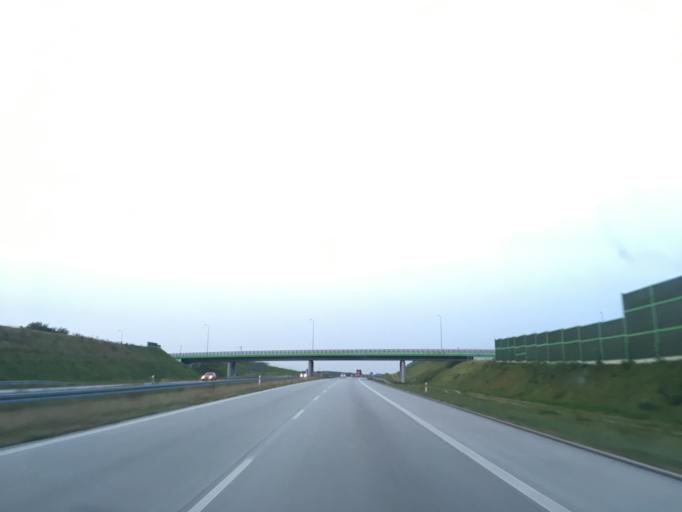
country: PL
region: Lodz Voivodeship
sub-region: Powiat zgierski
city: Strykow
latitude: 51.8572
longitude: 19.6592
